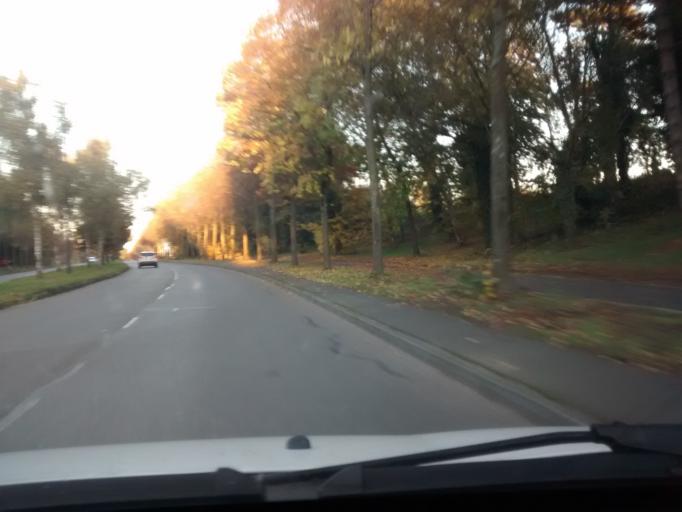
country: FR
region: Brittany
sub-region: Departement d'Ille-et-Vilaine
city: Rennes
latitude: 48.1281
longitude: -1.6822
